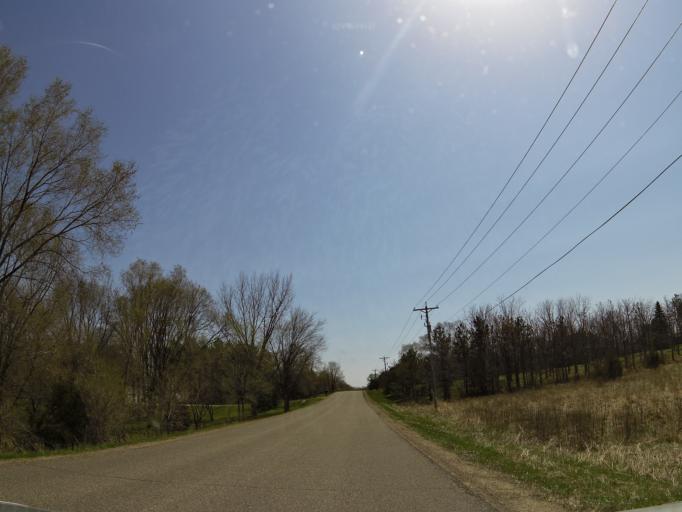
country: US
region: Wisconsin
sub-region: Saint Croix County
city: North Hudson
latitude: 44.9853
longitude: -92.7058
